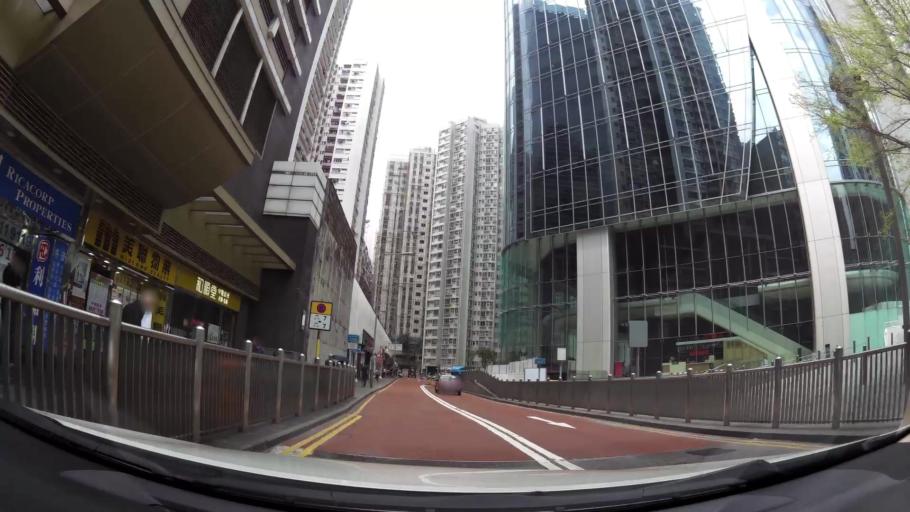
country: HK
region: Wanchai
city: Wan Chai
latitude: 22.2856
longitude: 114.2138
